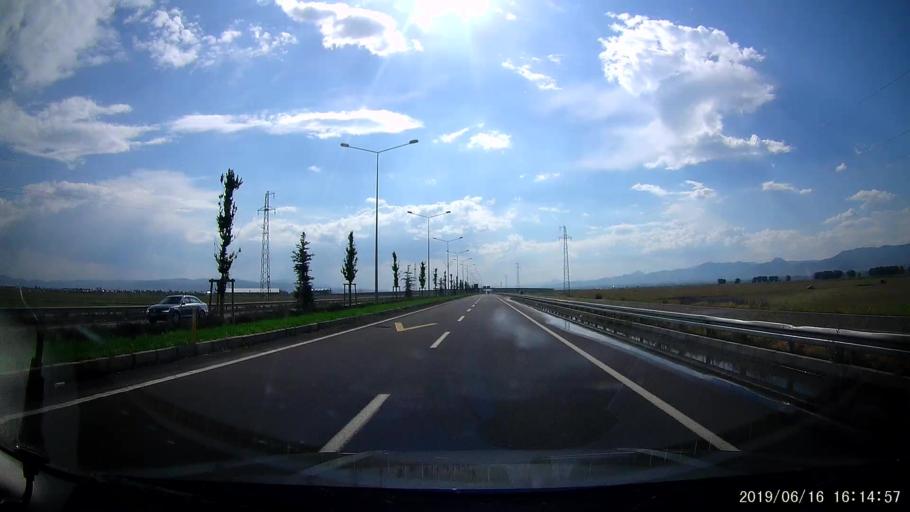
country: TR
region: Erzurum
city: Erzurum
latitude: 39.9614
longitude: 41.2365
